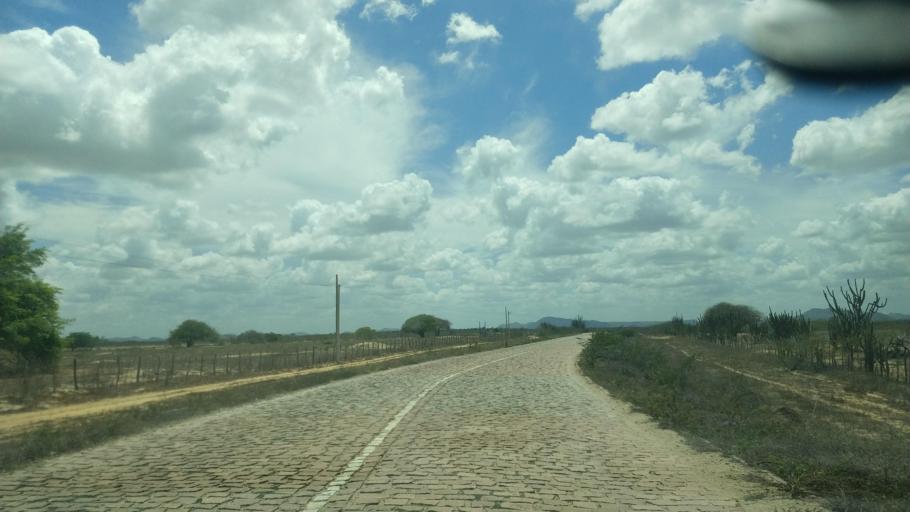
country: BR
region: Rio Grande do Norte
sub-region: Sao Paulo Do Potengi
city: Sao Paulo do Potengi
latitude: -5.9575
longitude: -35.8461
